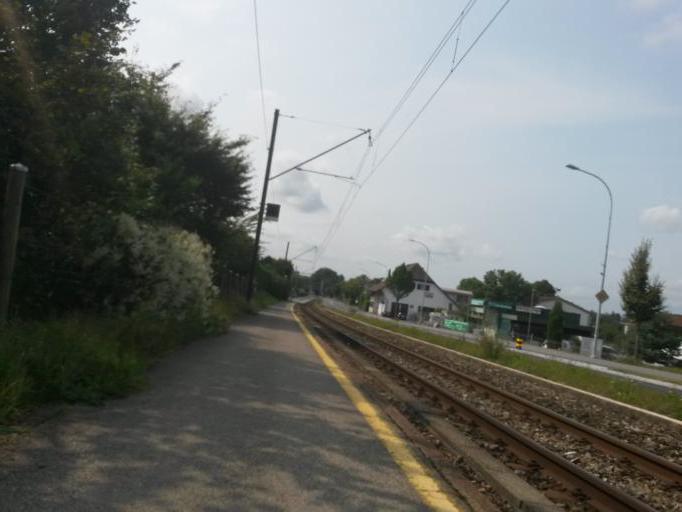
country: CH
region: Solothurn
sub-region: Bezirk Lebern
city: Riedholz
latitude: 47.2219
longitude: 7.5578
